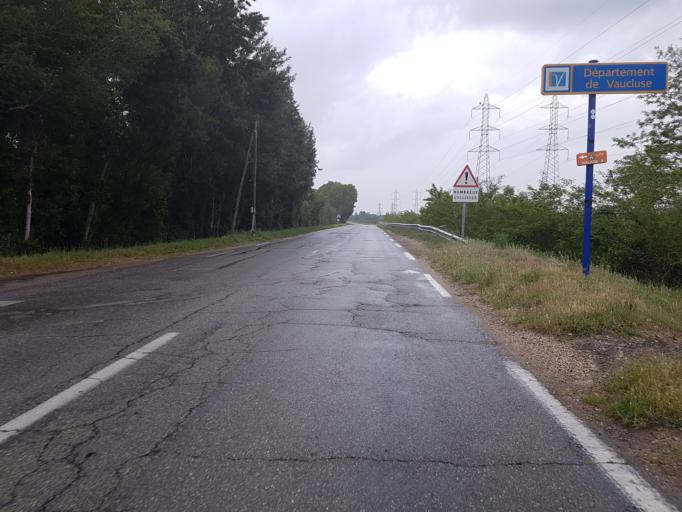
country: FR
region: Languedoc-Roussillon
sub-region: Departement du Gard
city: Villeneuve-les-Avignon
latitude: 43.9862
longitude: 4.8216
